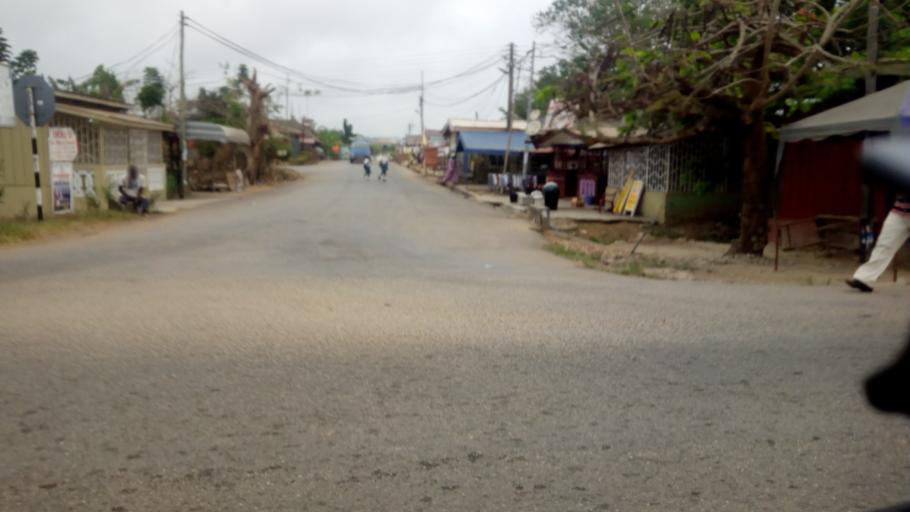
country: GH
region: Central
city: Cape Coast
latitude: 5.1193
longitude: -1.2670
